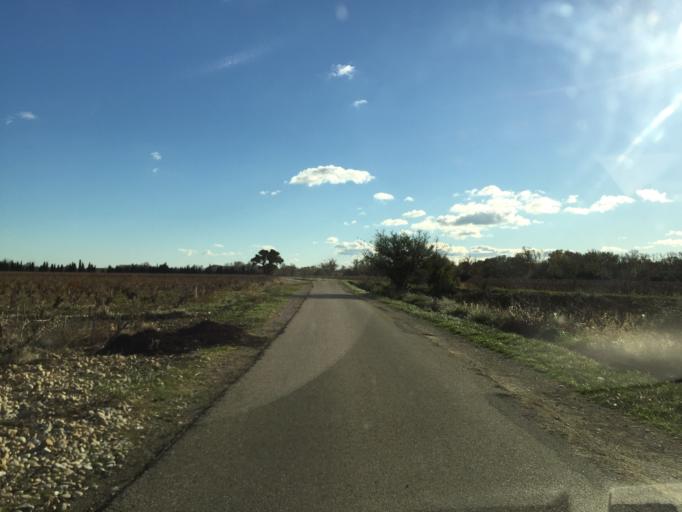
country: FR
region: Provence-Alpes-Cote d'Azur
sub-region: Departement du Vaucluse
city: Chateauneuf-du-Pape
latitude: 44.0362
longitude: 4.8373
